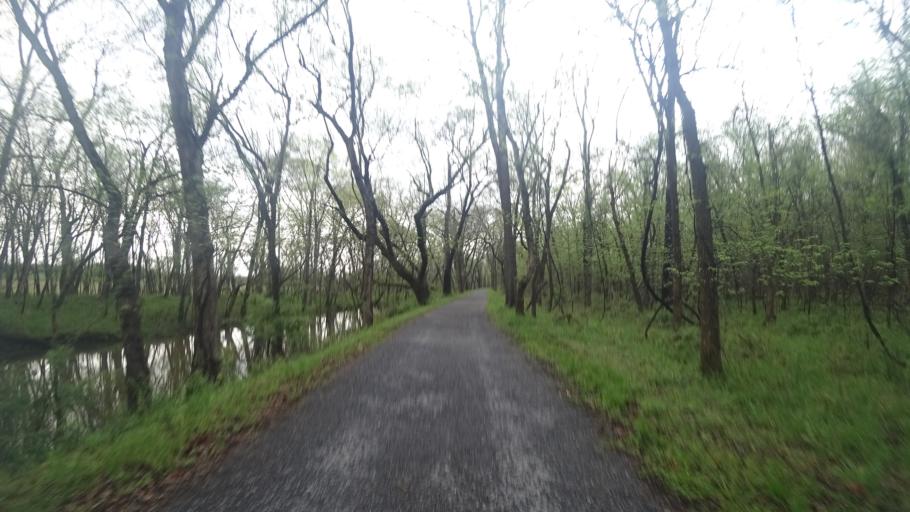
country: US
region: Virginia
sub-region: Loudoun County
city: Leesburg
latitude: 39.1221
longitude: -77.5074
